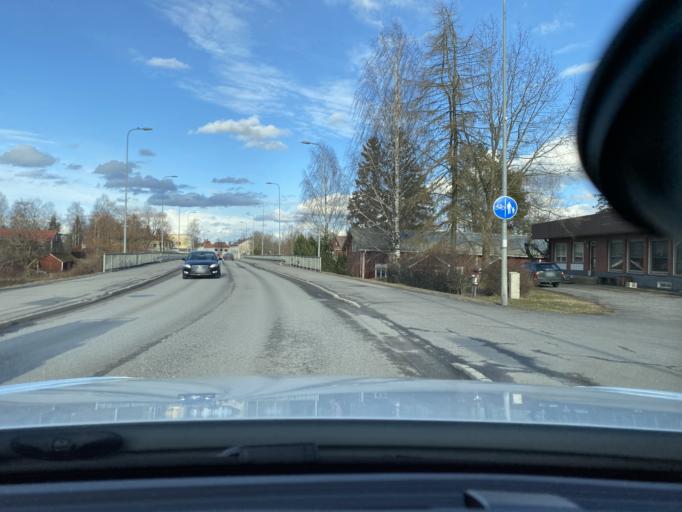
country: FI
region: Satakunta
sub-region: Pori
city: Huittinen
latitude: 61.1736
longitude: 22.6904
